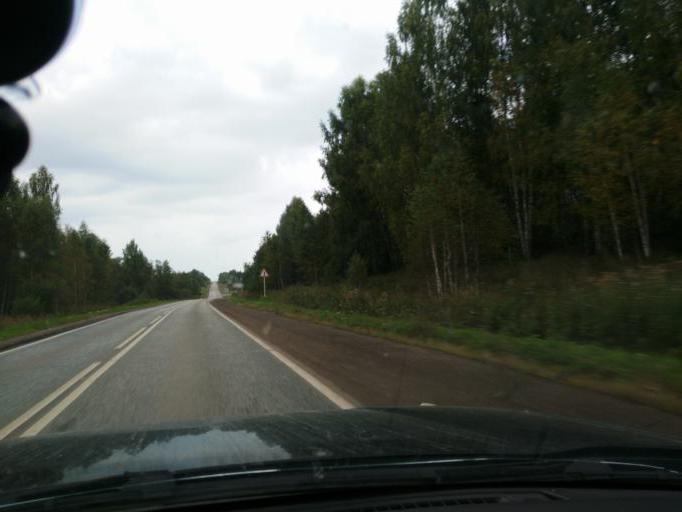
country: RU
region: Perm
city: Chernushka
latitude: 56.8413
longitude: 55.9843
